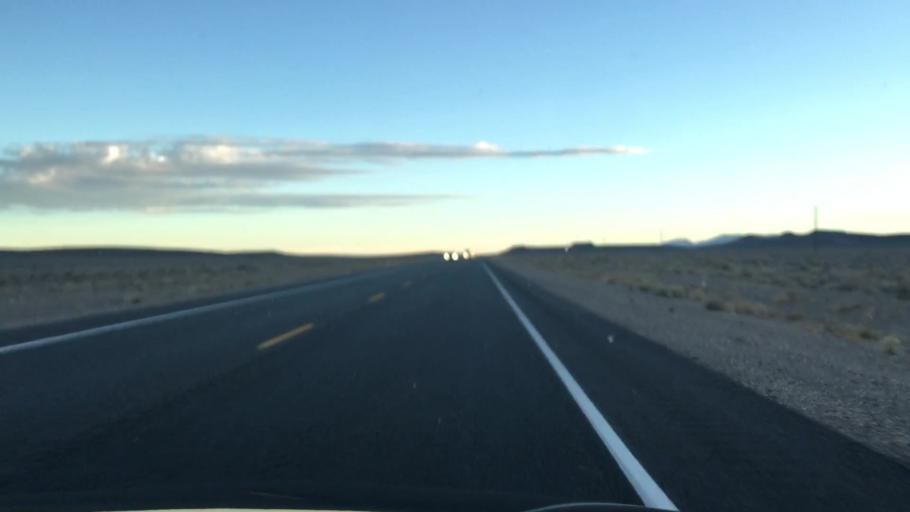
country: US
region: Nevada
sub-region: Esmeralda County
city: Goldfield
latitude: 37.4203
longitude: -117.1566
